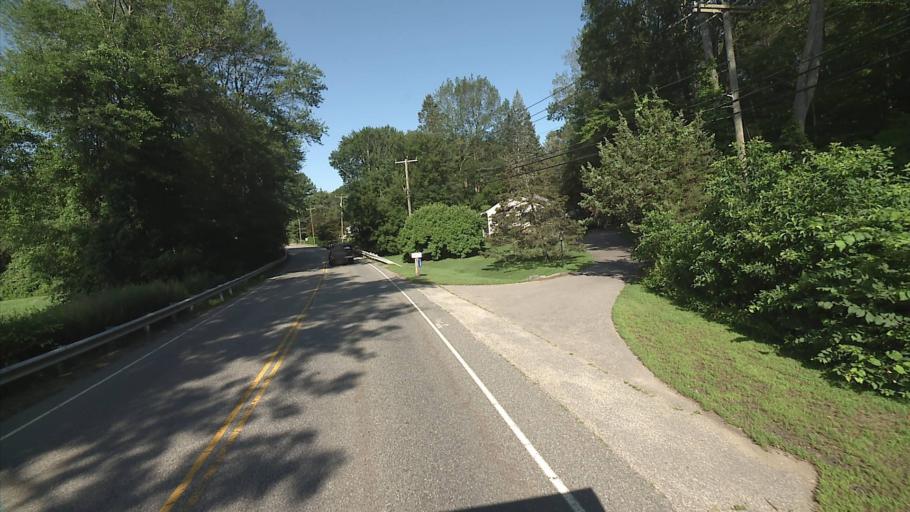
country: US
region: Connecticut
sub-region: New London County
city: Montville Center
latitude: 41.5443
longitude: -72.1787
